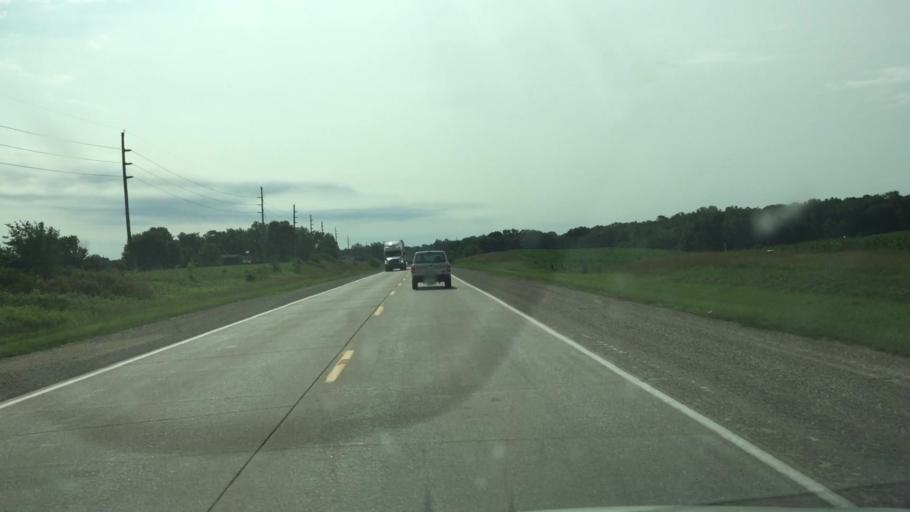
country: US
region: Illinois
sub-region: Hancock County
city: Nauvoo
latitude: 40.6314
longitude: -91.4977
